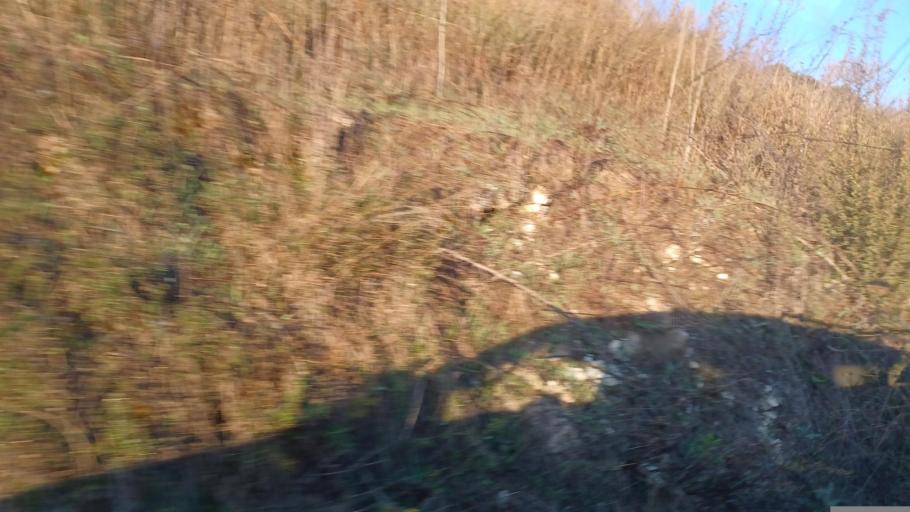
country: CY
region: Pafos
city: Mesogi
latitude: 34.8659
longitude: 32.5098
